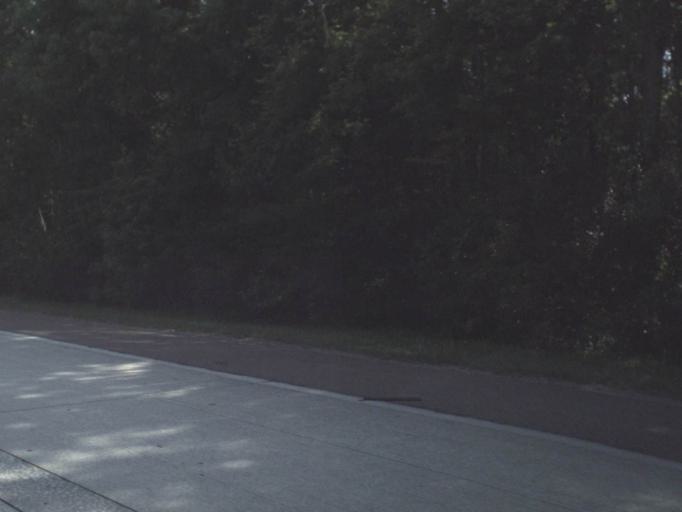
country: US
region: Florida
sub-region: Nassau County
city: Yulee
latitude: 30.4867
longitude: -81.6424
